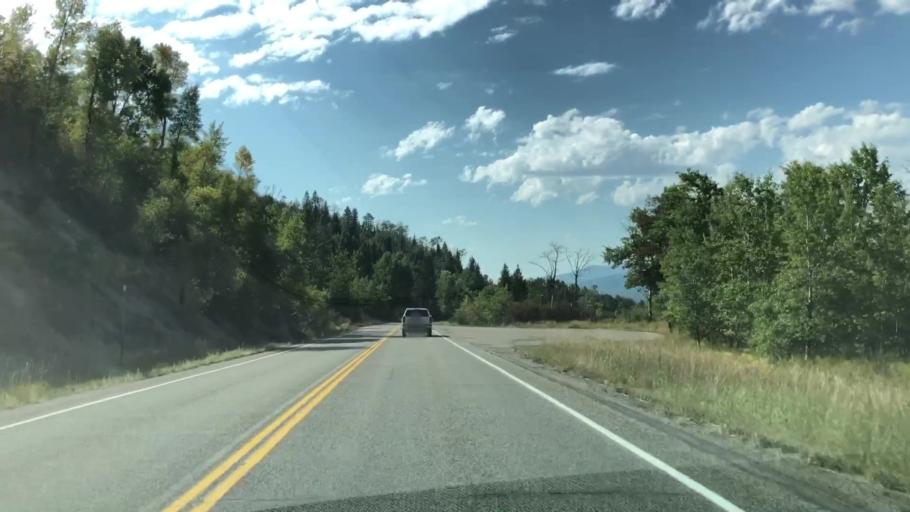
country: US
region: Idaho
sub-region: Teton County
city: Victor
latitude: 43.2759
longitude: -111.1143
